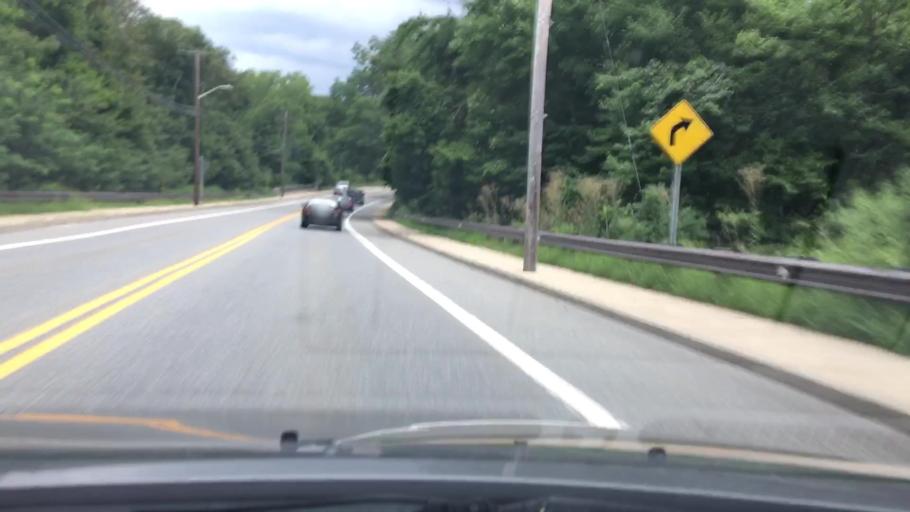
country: US
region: Rhode Island
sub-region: Providence County
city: Cumberland
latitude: 41.9796
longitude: -71.3949
